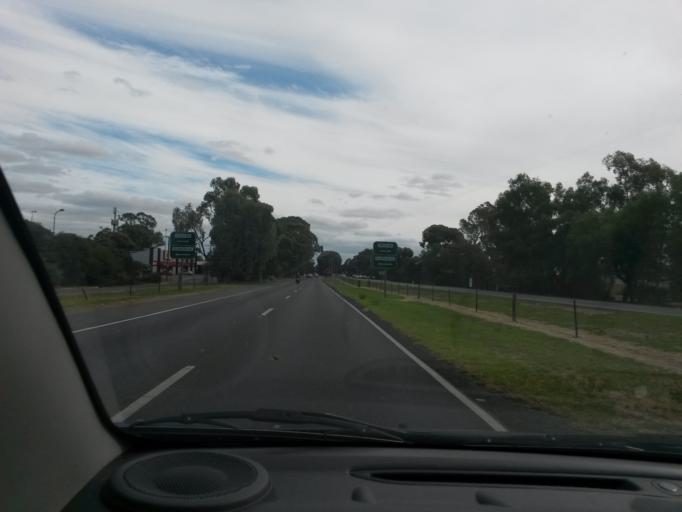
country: AU
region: South Australia
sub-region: Salisbury
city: Salisbury
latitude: -34.7810
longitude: 138.6564
